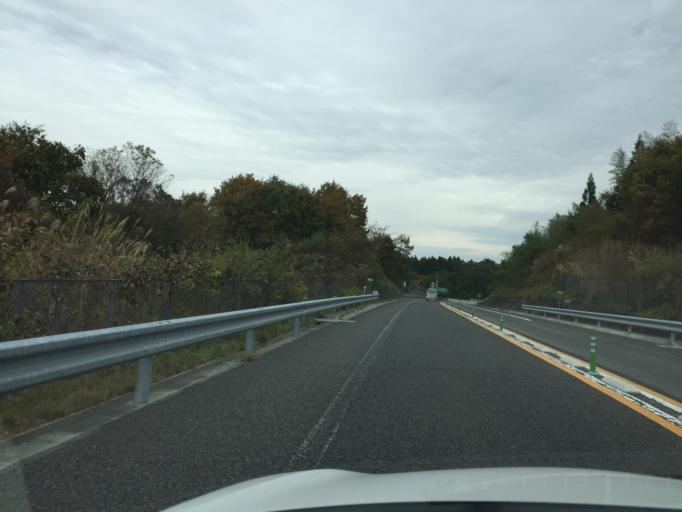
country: JP
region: Fukushima
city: Ishikawa
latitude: 37.2237
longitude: 140.5449
